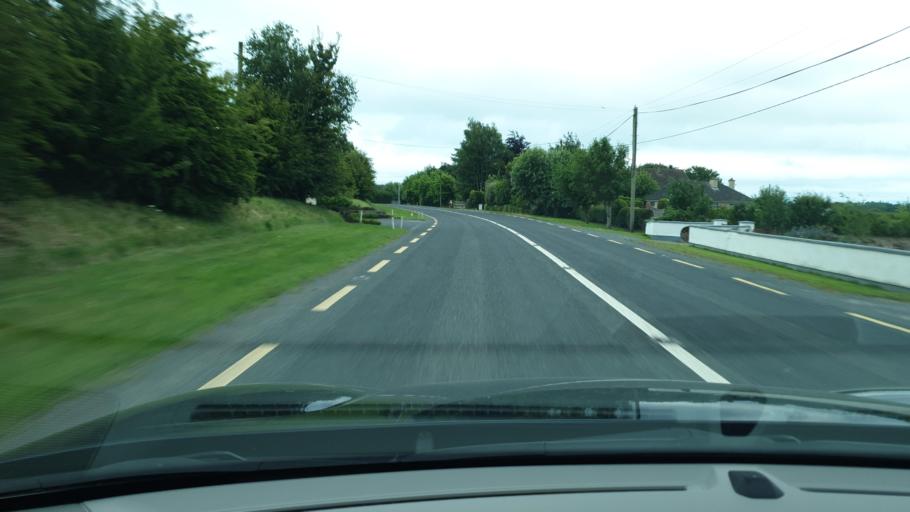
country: IE
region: Leinster
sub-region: An Mhi
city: Dunshaughlin
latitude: 53.4878
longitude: -6.5728
